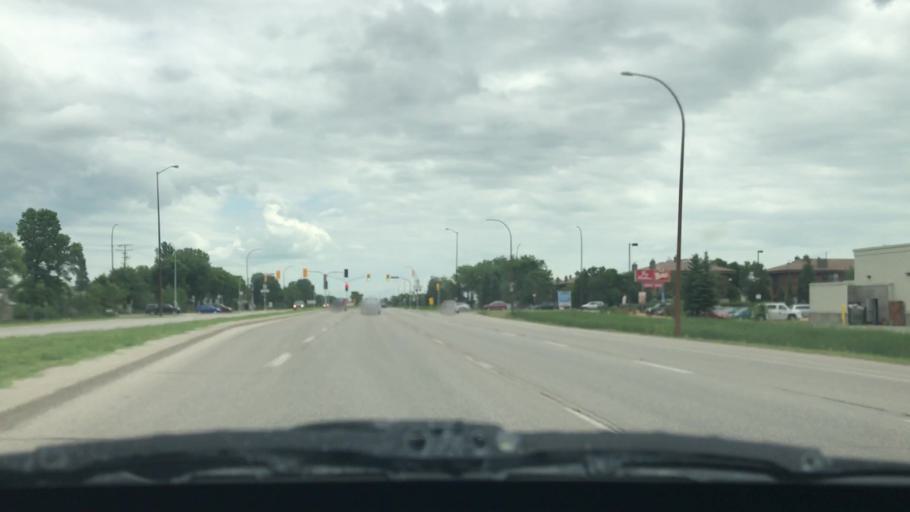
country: CA
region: Manitoba
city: Winnipeg
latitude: 49.8560
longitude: -97.0674
